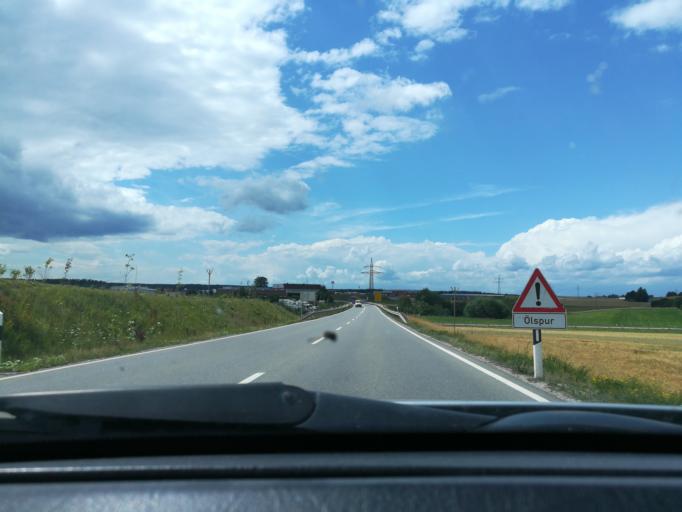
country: DE
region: Baden-Wuerttemberg
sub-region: Freiburg Region
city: Dunningen
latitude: 48.2202
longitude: 8.5096
